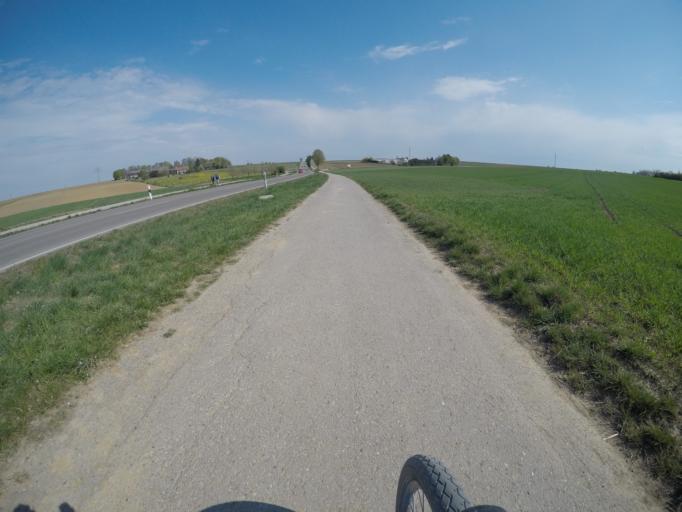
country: DE
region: Baden-Wuerttemberg
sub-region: Regierungsbezirk Stuttgart
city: Ditzingen
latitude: 48.8357
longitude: 9.0756
